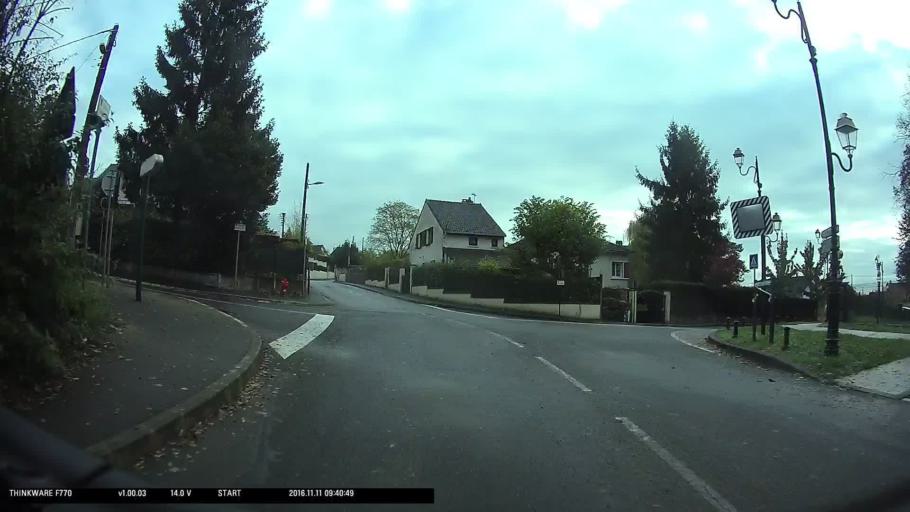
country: FR
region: Ile-de-France
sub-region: Departement du Val-d'Oise
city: Osny
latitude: 49.0653
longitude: 2.0651
